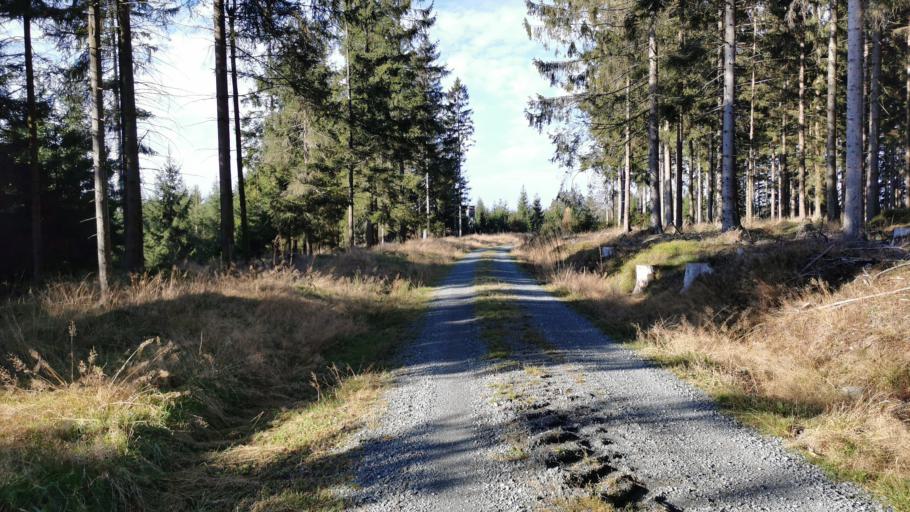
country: DE
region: Bavaria
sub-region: Upper Franconia
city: Tschirn
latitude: 50.4254
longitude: 11.4557
